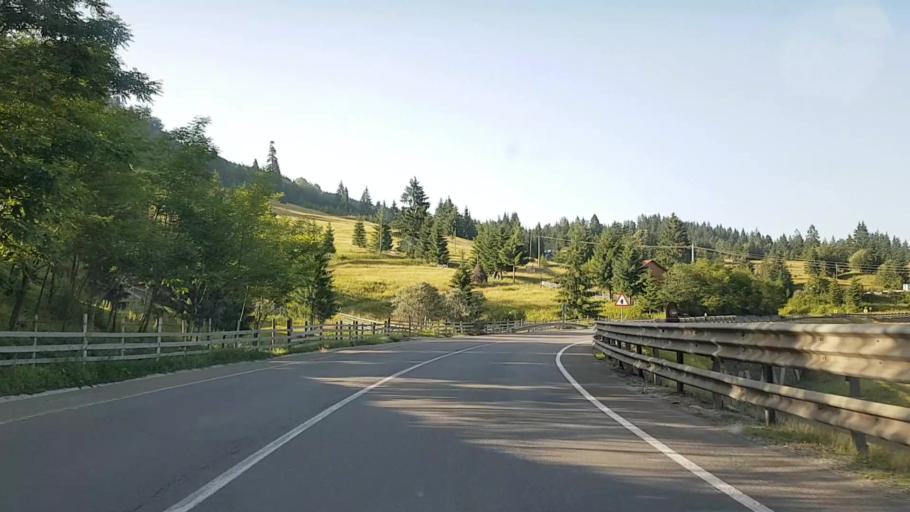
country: RO
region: Bistrita-Nasaud
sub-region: Comuna Lunca Ilvei
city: Lunca Ilvei
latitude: 47.2239
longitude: 24.9562
